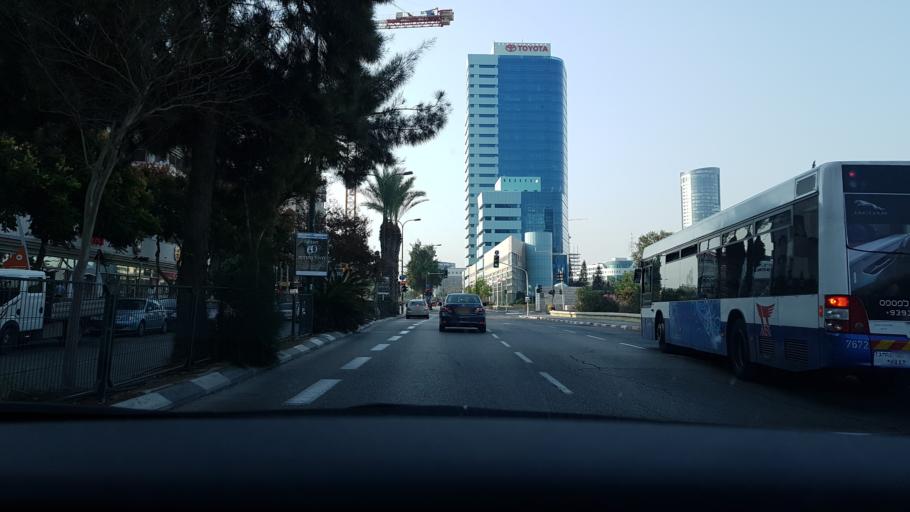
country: IL
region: Tel Aviv
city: Tel Aviv
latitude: 32.0679
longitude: 34.7931
